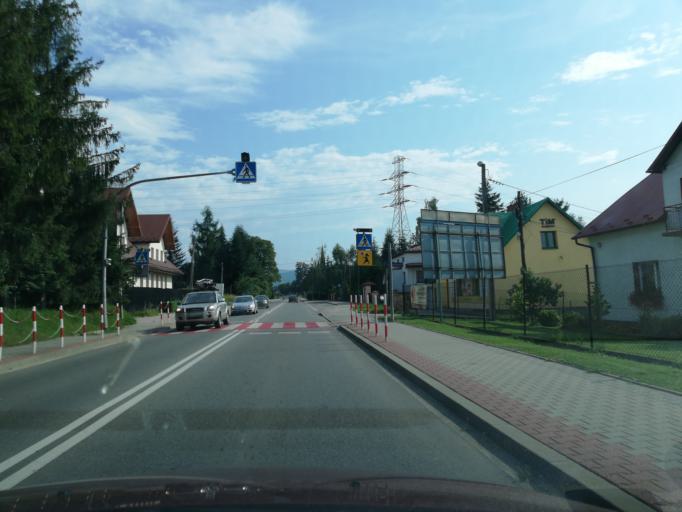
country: PL
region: Lesser Poland Voivodeship
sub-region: Powiat nowosadecki
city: Nawojowa
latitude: 49.5858
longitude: 20.7257
